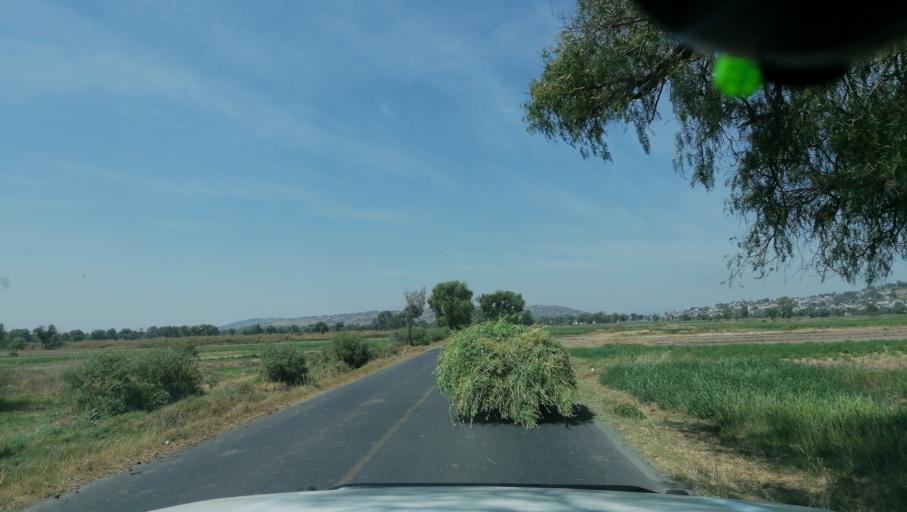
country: MX
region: Tlaxcala
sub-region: Tetlatlahuca
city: Tetlatlahuca
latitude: 19.2161
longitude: -98.2880
